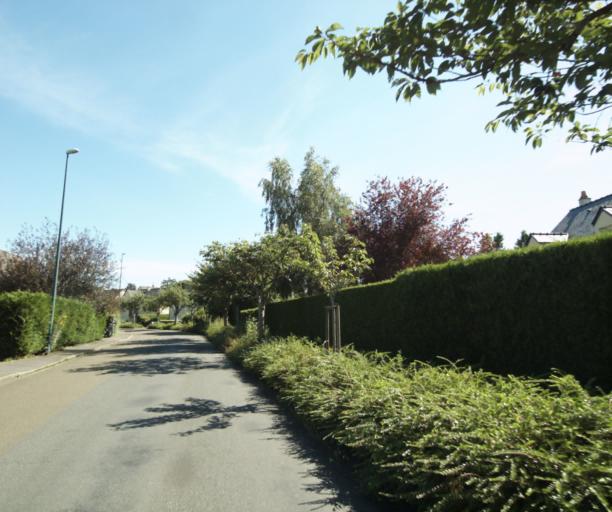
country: FR
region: Pays de la Loire
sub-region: Departement de la Mayenne
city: Saint-Berthevin
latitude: 48.0635
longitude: -0.8017
